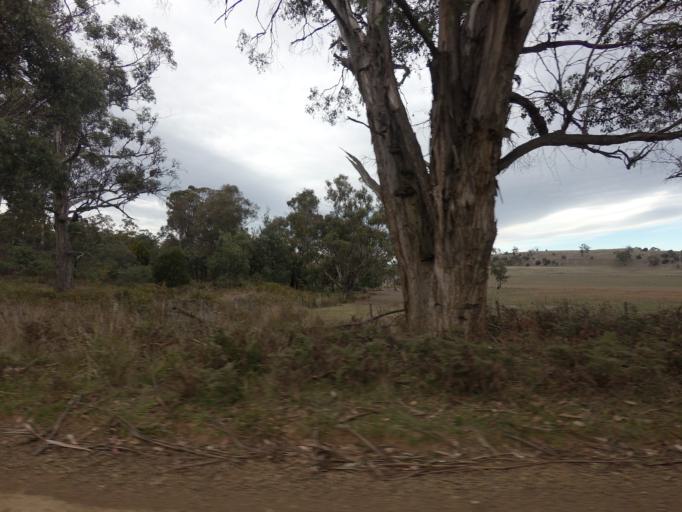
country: AU
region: Tasmania
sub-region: Derwent Valley
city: New Norfolk
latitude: -42.5632
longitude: 146.9383
